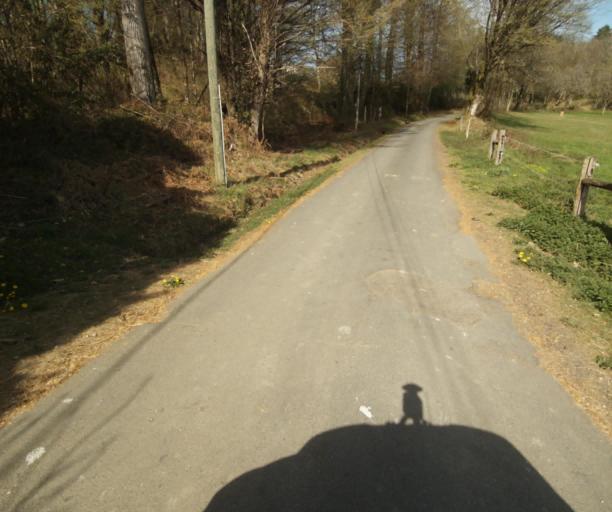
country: FR
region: Limousin
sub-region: Departement de la Correze
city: Naves
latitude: 45.3480
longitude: 1.7625
